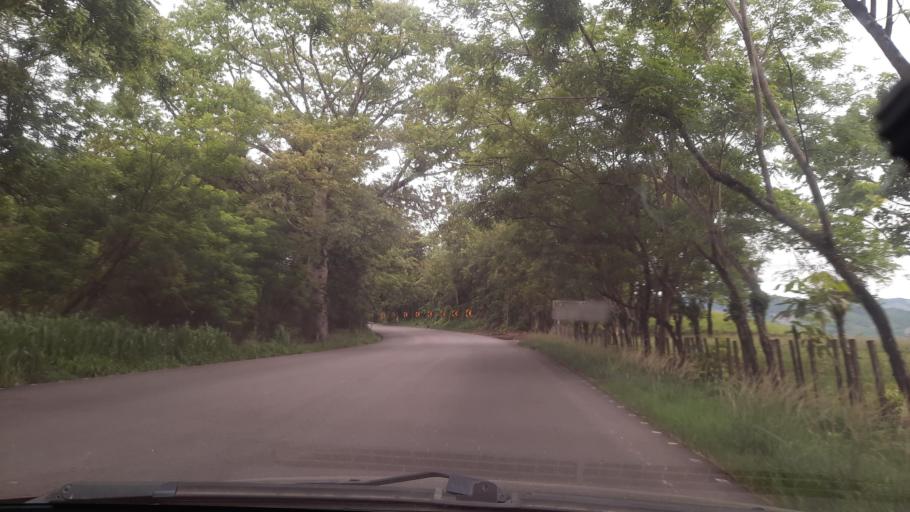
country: GT
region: Izabal
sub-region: Municipio de Los Amates
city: Los Amates
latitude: 15.2510
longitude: -89.1253
